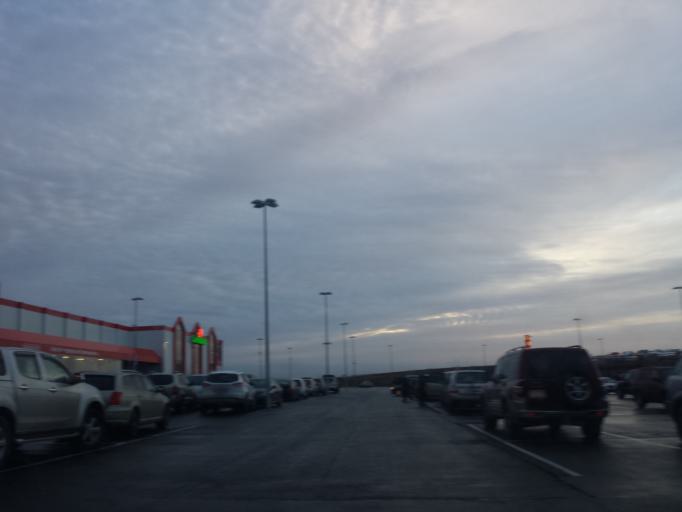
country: IS
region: Capital Region
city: Mosfellsbaer
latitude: 64.1412
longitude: -21.7537
